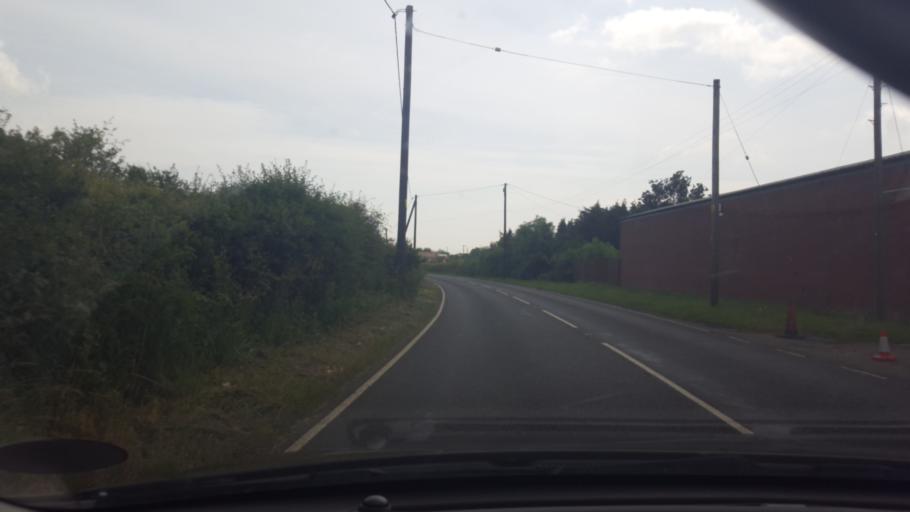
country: GB
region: England
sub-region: Essex
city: Mistley
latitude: 51.8928
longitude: 1.1039
